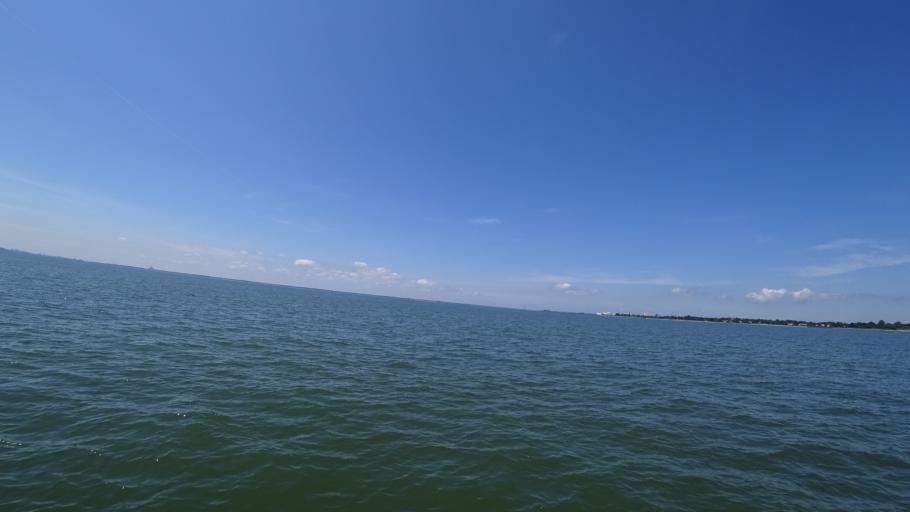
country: US
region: Virginia
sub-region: City of Newport News
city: Newport News
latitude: 36.9827
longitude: -76.3821
